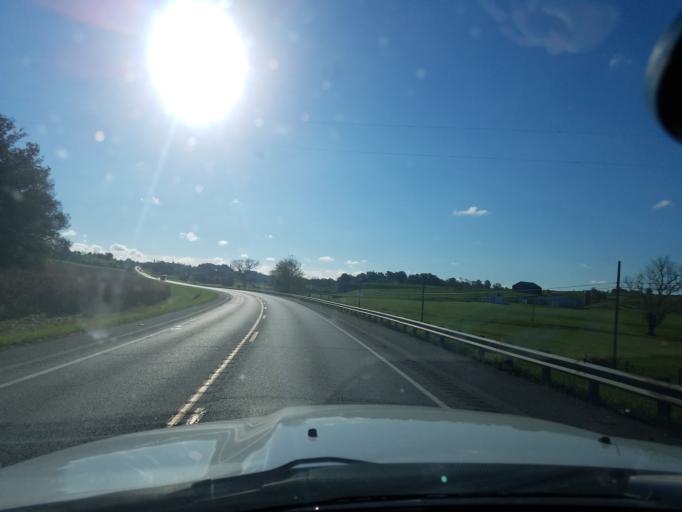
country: US
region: Kentucky
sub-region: Washington County
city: Springfield
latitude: 37.7179
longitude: -85.2784
